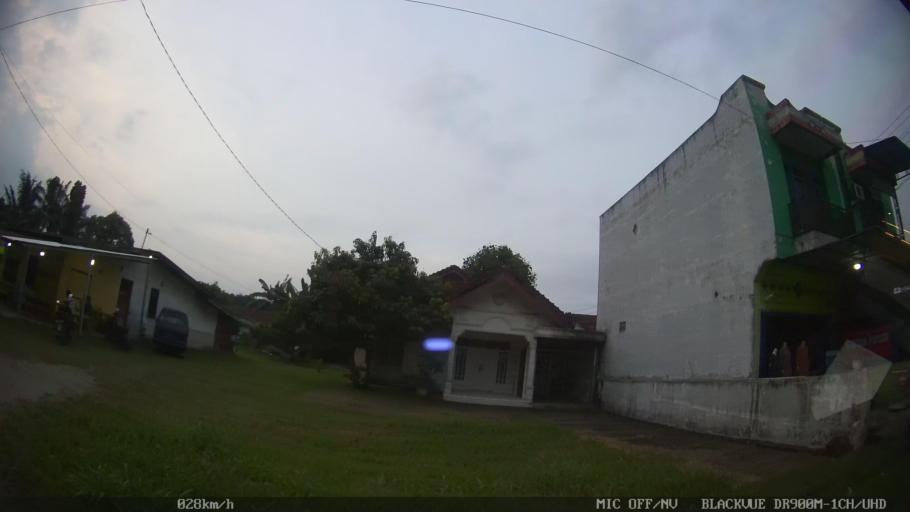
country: ID
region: North Sumatra
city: Sunggal
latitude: 3.5856
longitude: 98.5932
